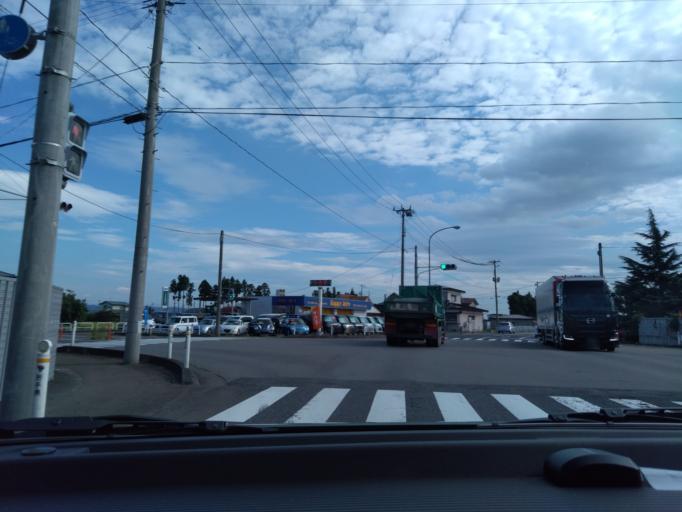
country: JP
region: Iwate
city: Hanamaki
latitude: 39.4446
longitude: 141.0989
